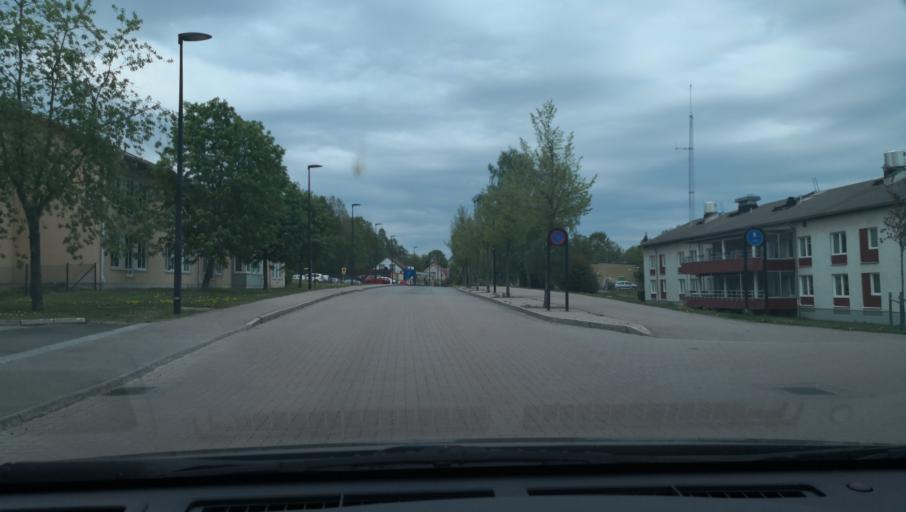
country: SE
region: Vaestmanland
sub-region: Skinnskattebergs Kommun
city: Skinnskatteberg
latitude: 59.8280
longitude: 15.6921
